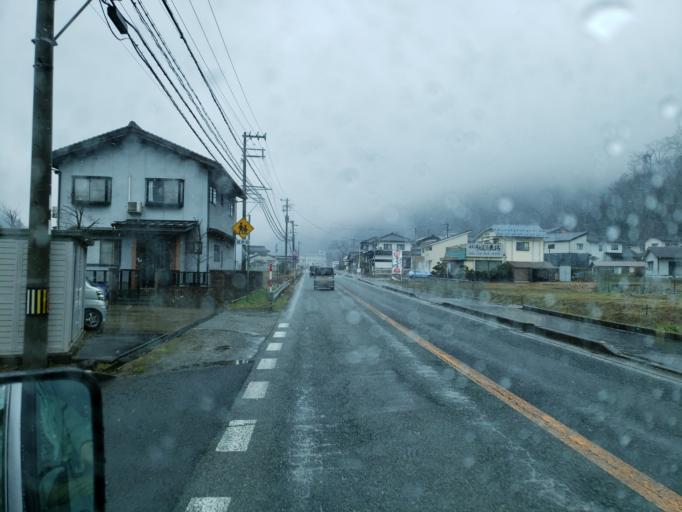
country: JP
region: Hyogo
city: Toyooka
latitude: 35.3860
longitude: 134.6940
